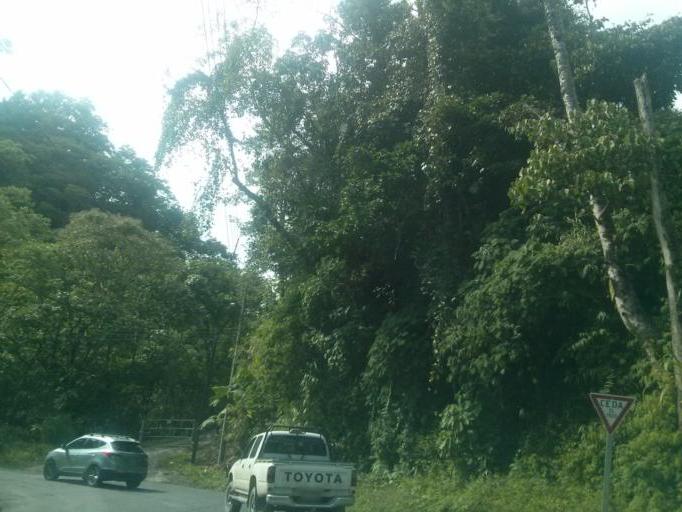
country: CR
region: Cartago
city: Cot
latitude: 9.9228
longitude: -83.7942
